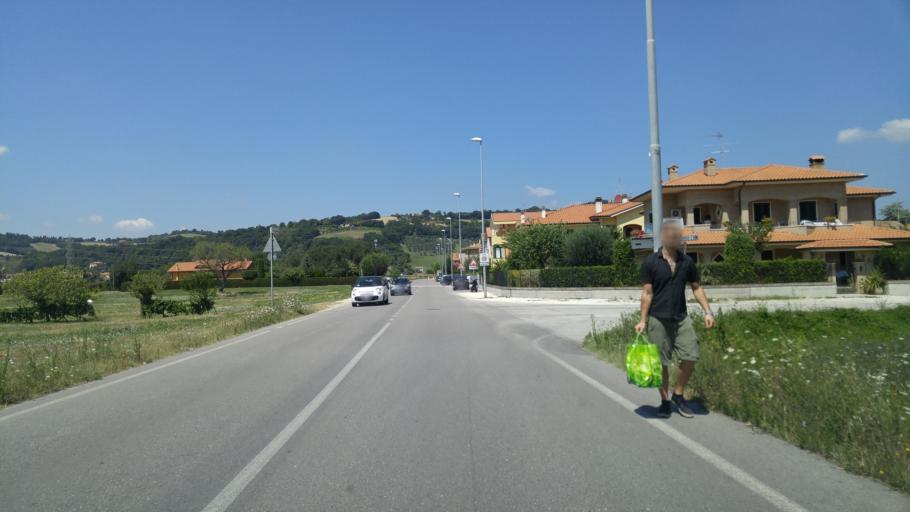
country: IT
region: The Marches
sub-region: Provincia di Pesaro e Urbino
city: Rosciano
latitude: 43.8031
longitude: 12.9899
